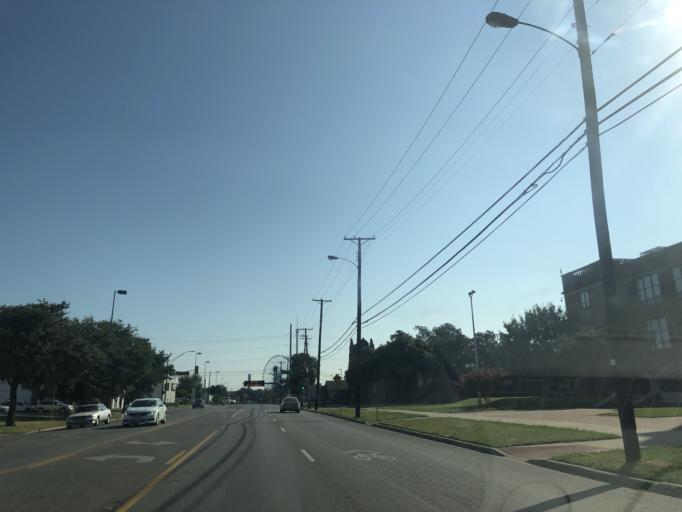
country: US
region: Texas
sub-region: Dallas County
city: Dallas
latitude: 32.7715
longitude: -96.7657
